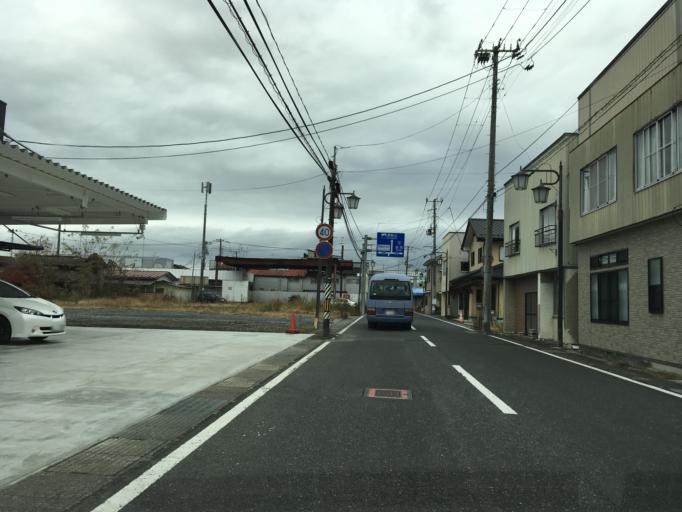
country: JP
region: Iwate
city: Ichinoseki
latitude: 38.8308
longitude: 140.9929
